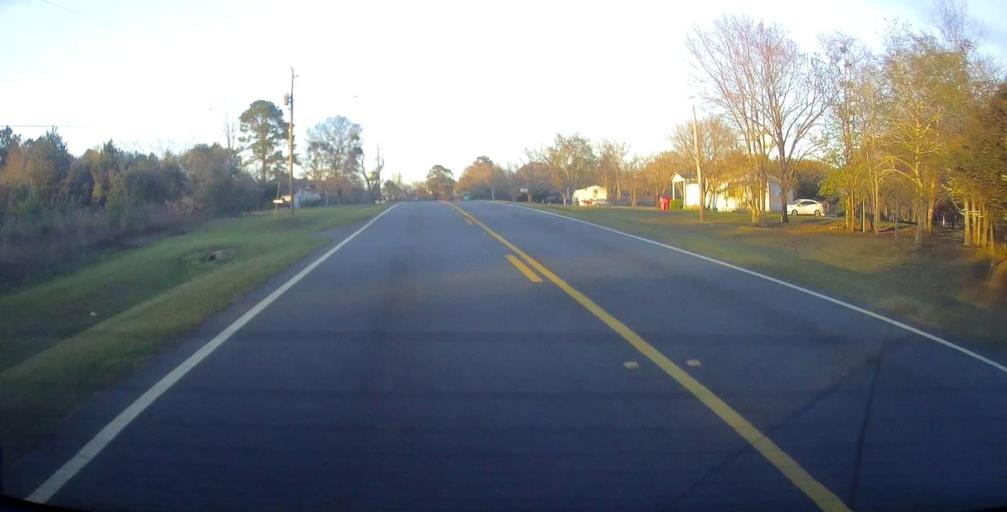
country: US
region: Georgia
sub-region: Dodge County
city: Chester
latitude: 32.3350
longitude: -83.0452
